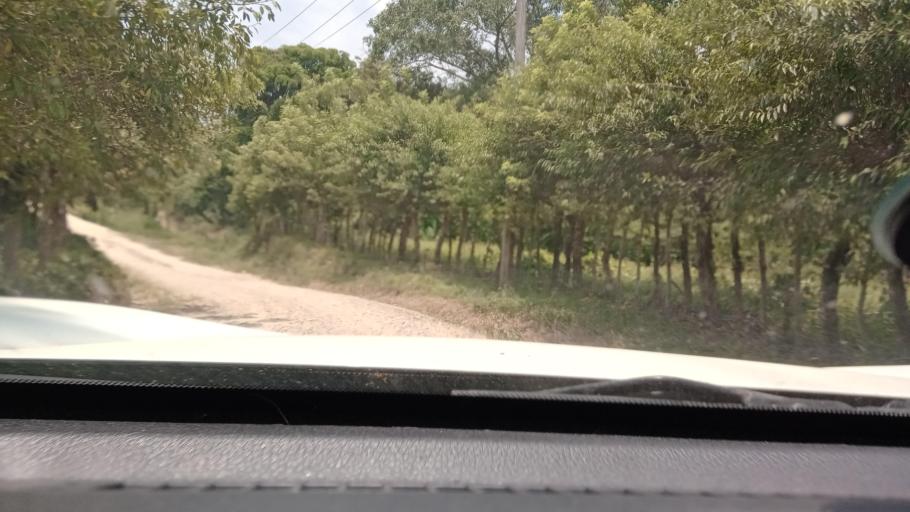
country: MX
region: Tabasco
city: Chontalpa
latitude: 17.5690
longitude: -93.7117
